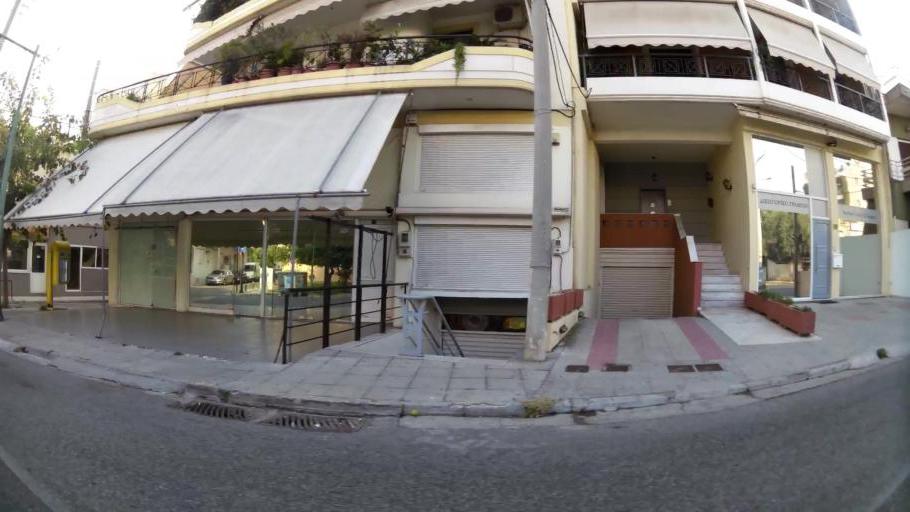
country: GR
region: Attica
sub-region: Nomarchia Athinas
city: Ilion
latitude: 38.0360
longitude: 23.7018
